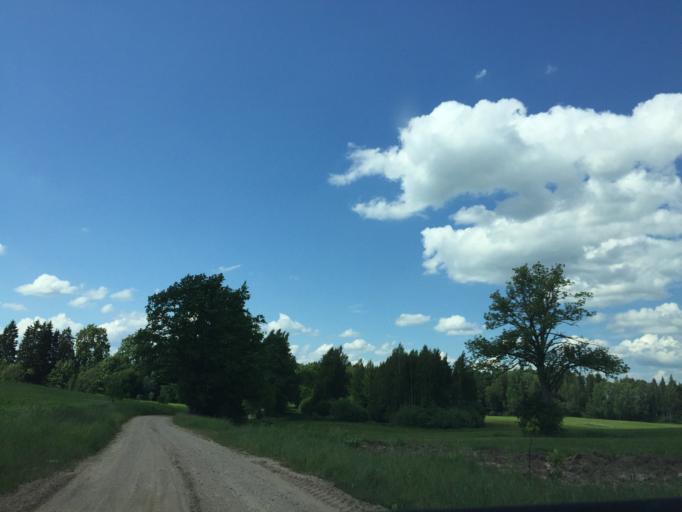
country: LV
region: Priekuli
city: Priekuli
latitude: 57.2377
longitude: 25.4189
